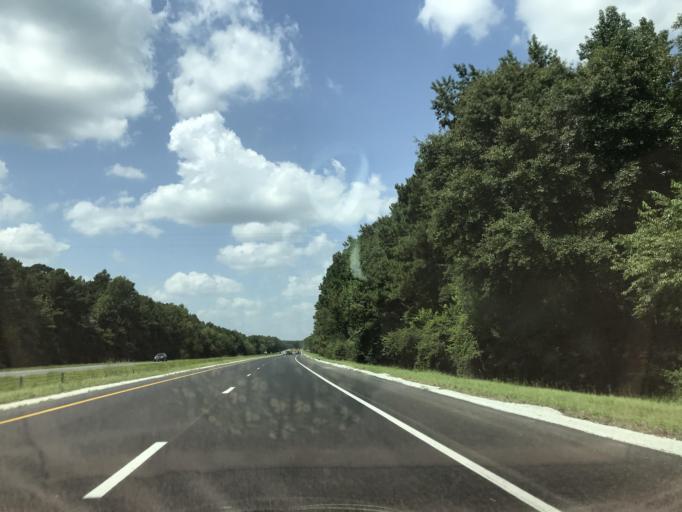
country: US
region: North Carolina
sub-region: Duplin County
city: Warsaw
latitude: 34.9497
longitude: -78.0850
